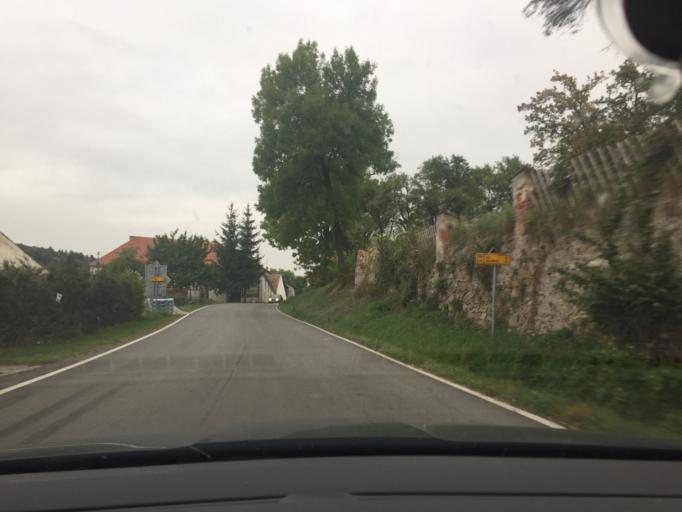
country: CZ
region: Jihocesky
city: Brloh
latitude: 48.9297
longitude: 14.2206
